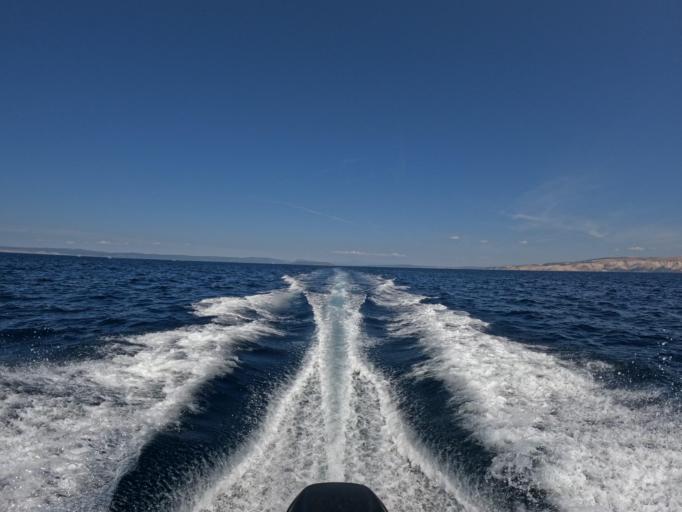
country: HR
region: Primorsko-Goranska
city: Lopar
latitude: 44.8824
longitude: 14.6553
